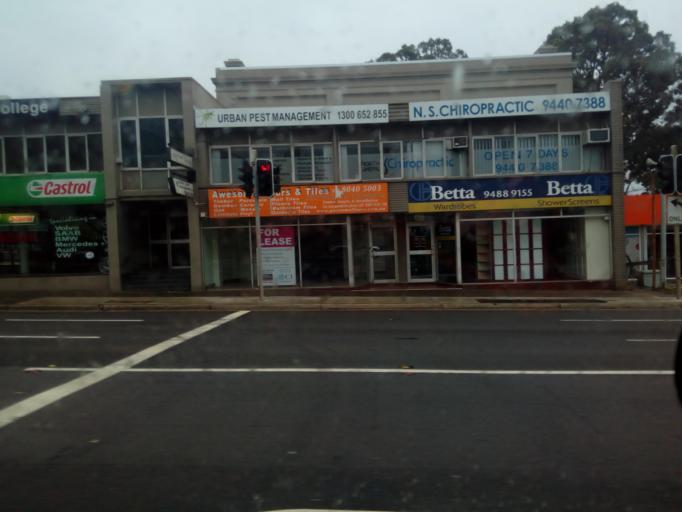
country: AU
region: New South Wales
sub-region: City of Sydney
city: Pymble
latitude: -33.7491
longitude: 151.1460
